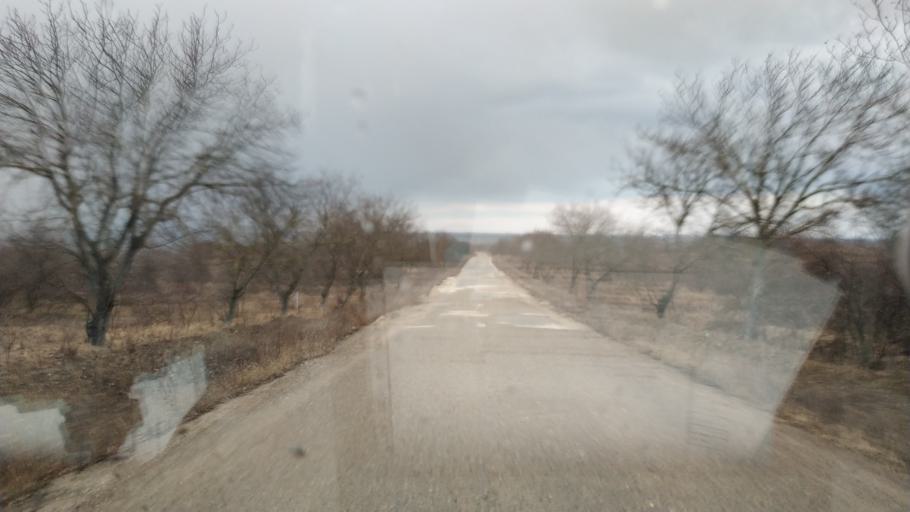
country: MD
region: Telenesti
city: Grigoriopol
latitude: 47.0719
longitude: 29.3083
